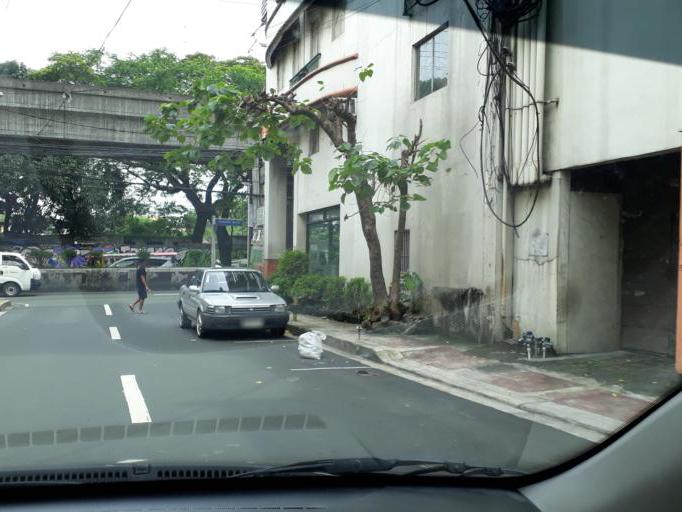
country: PH
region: Metro Manila
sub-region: Quezon City
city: Quezon City
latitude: 14.6260
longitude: 121.0582
